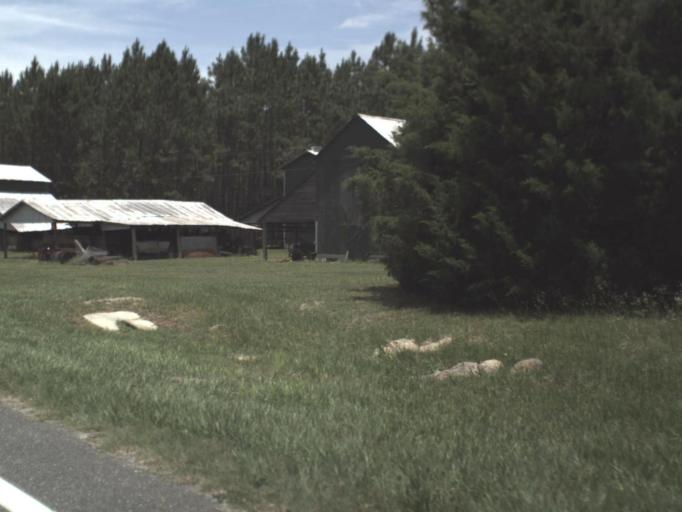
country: US
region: Florida
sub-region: Lafayette County
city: Mayo
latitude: 30.1559
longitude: -83.1595
